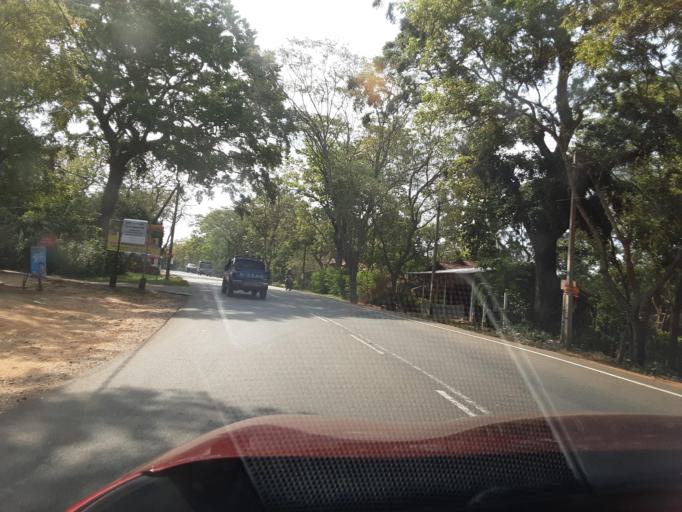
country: LK
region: Uva
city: Haputale
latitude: 6.3558
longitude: 81.1907
